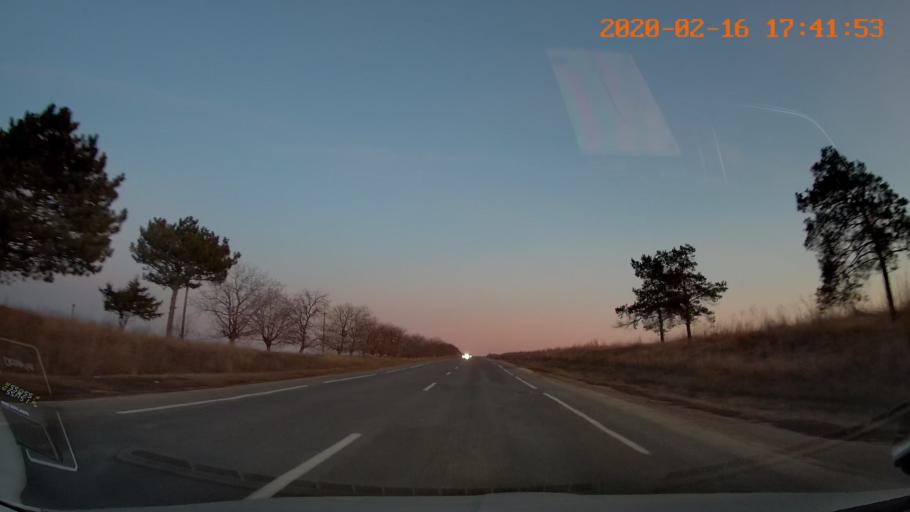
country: MD
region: Riscani
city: Riscani
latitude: 48.0267
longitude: 27.5390
